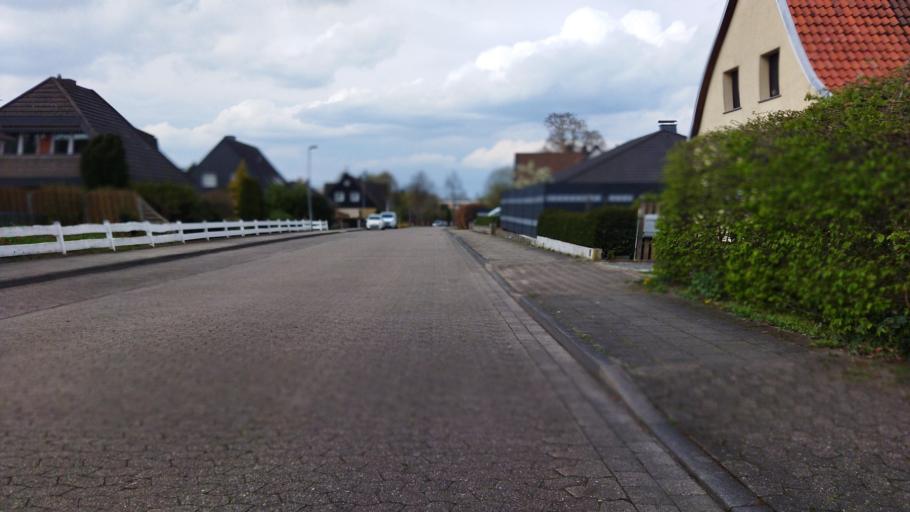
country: DE
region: Lower Saxony
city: Verden
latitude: 52.9324
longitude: 9.2270
